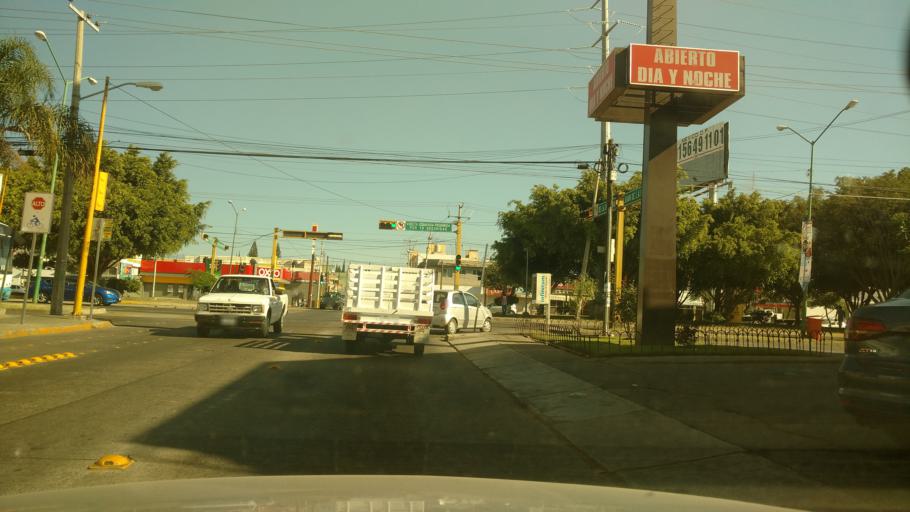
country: MX
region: Guanajuato
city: Leon
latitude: 21.1514
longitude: -101.6730
